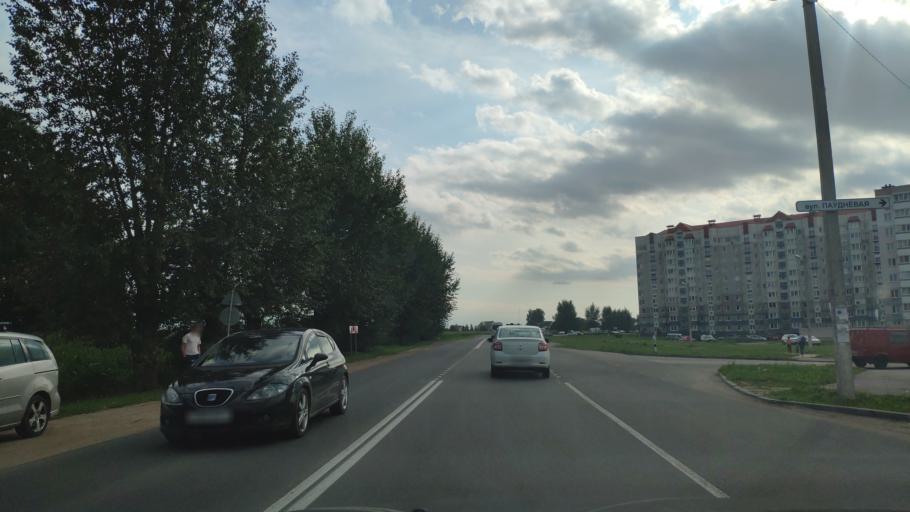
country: BY
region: Minsk
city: Azyartso
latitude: 53.8435
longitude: 27.4084
